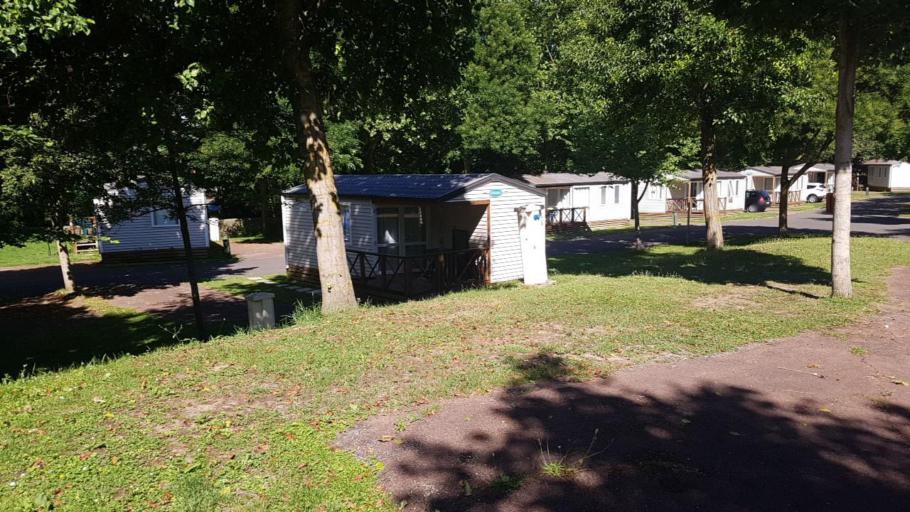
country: FR
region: Ile-de-France
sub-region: Departement de Seine-et-Marne
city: Annet-sur-Marne
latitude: 48.9129
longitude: 2.7296
